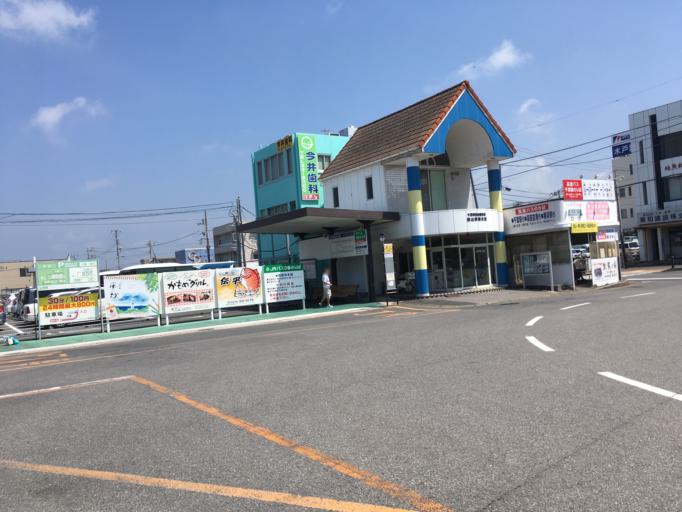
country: JP
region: Chiba
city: Tateyama
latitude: 34.9963
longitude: 139.8622
